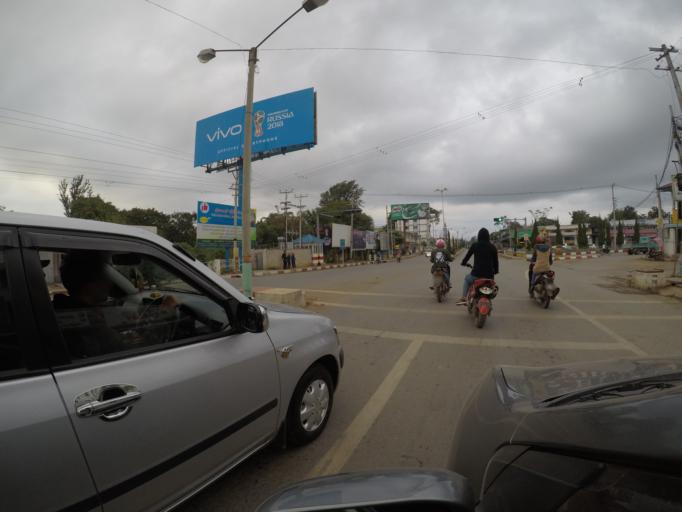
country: MM
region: Shan
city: Taunggyi
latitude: 20.7975
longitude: 97.0370
